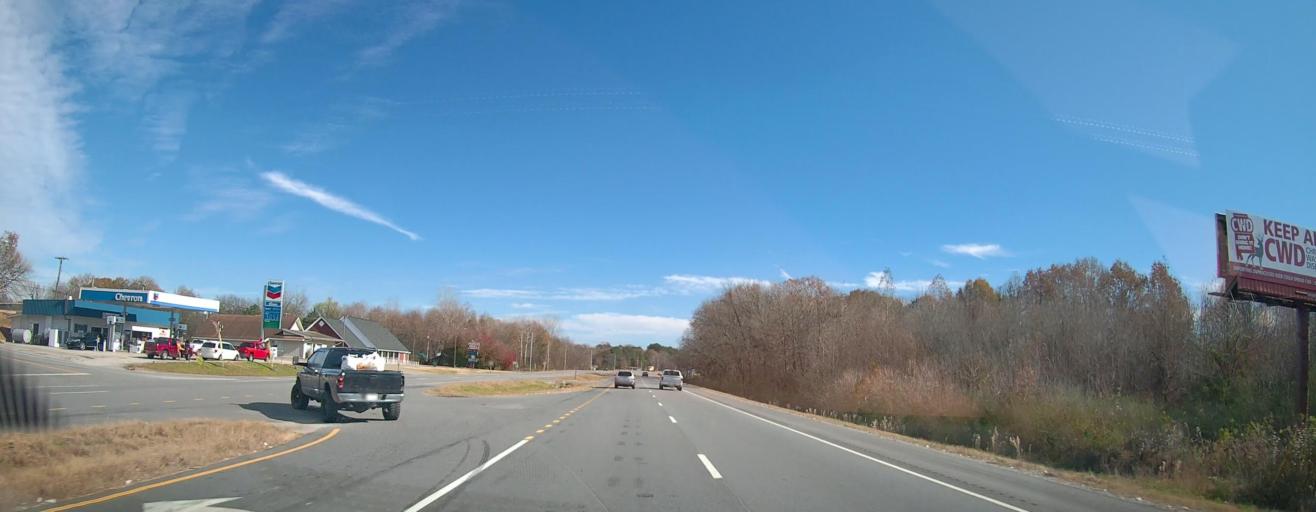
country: US
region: Alabama
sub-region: Colbert County
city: Cherokee
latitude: 34.7544
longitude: -87.9740
